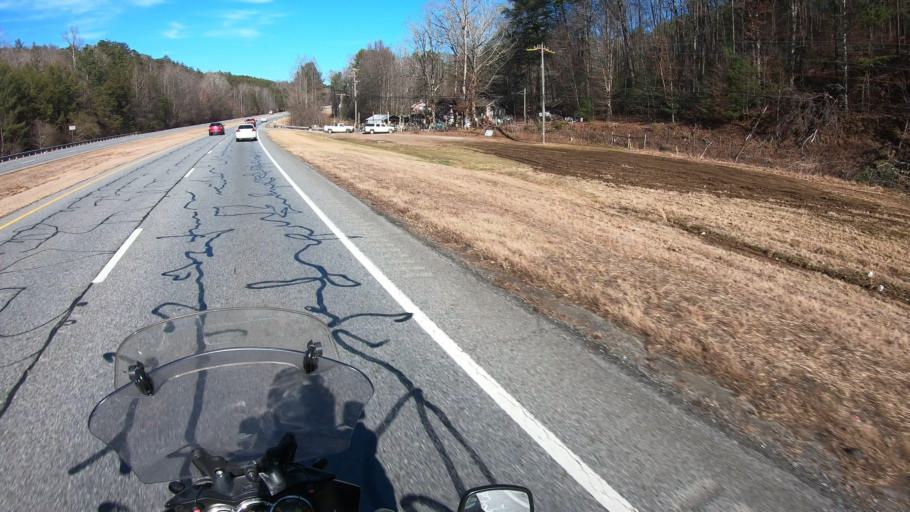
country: US
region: Georgia
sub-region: Gilmer County
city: Ellijay
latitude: 34.7656
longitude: -84.3997
